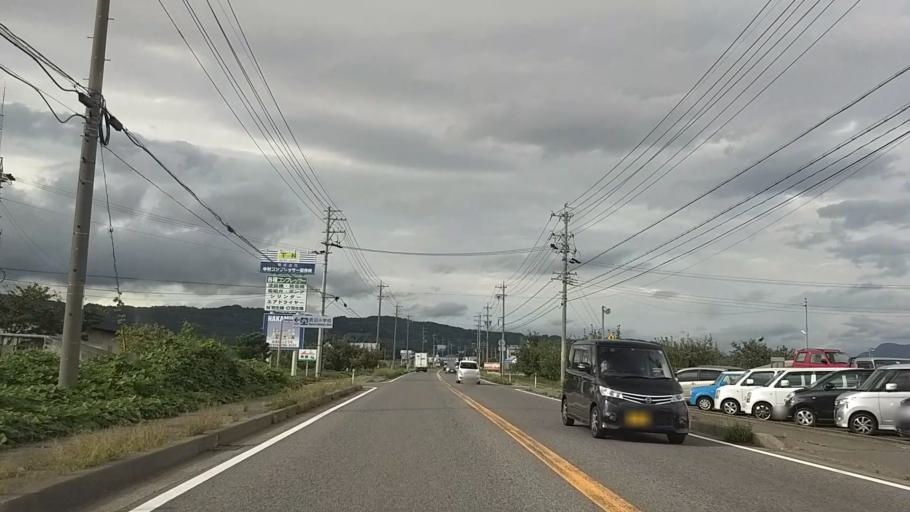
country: JP
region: Nagano
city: Suzaka
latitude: 36.6893
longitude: 138.2682
